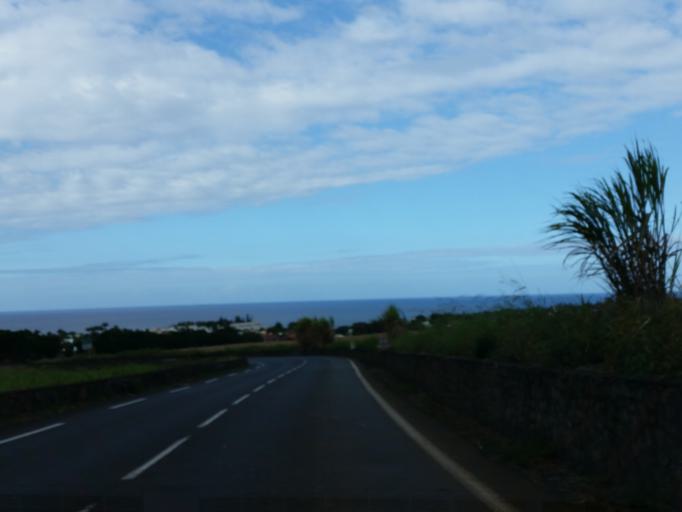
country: RE
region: Reunion
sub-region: Reunion
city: Sainte-Marie
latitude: -20.9058
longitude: 55.5429
